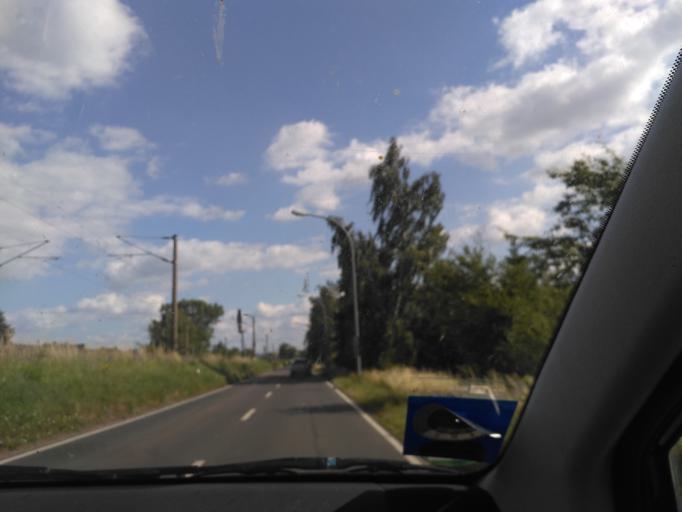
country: DE
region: Saxony
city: Weinbohla
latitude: 51.1654
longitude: 13.5590
